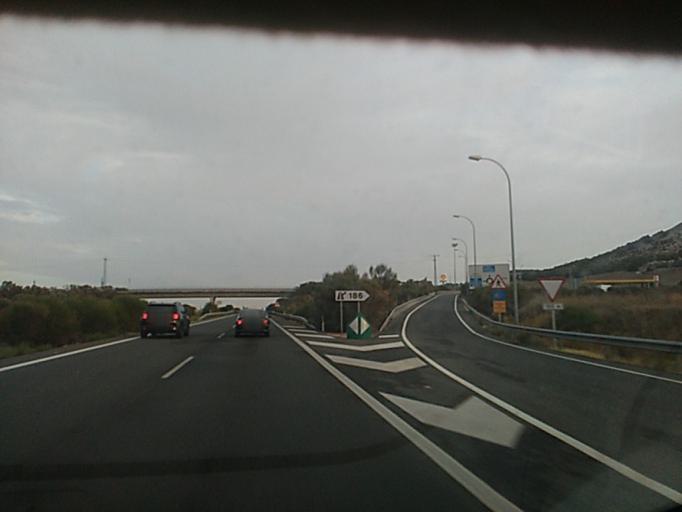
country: ES
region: Castille and Leon
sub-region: Provincia de Valladolid
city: Bercero
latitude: 41.5238
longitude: -5.0411
